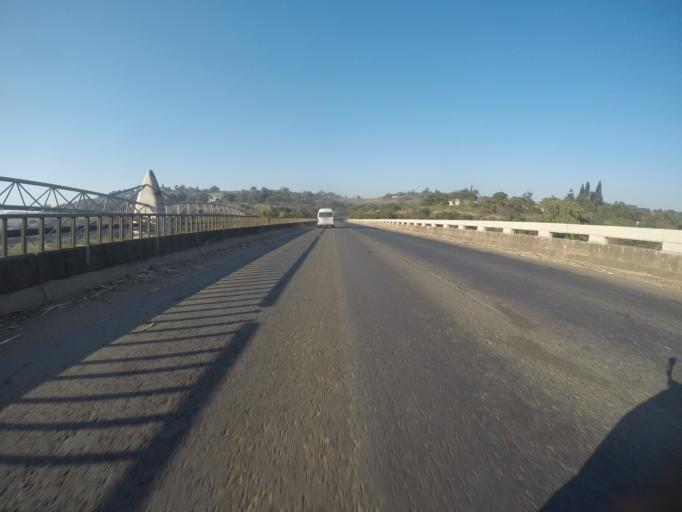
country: ZA
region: KwaZulu-Natal
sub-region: iLembe District Municipality
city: Stanger
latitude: -29.3831
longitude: 31.2531
